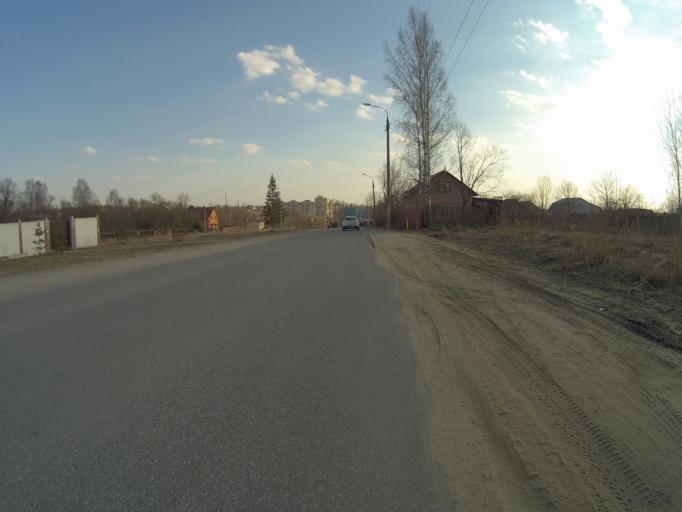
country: RU
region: Vladimir
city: Kommunar
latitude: 56.0678
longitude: 40.4887
